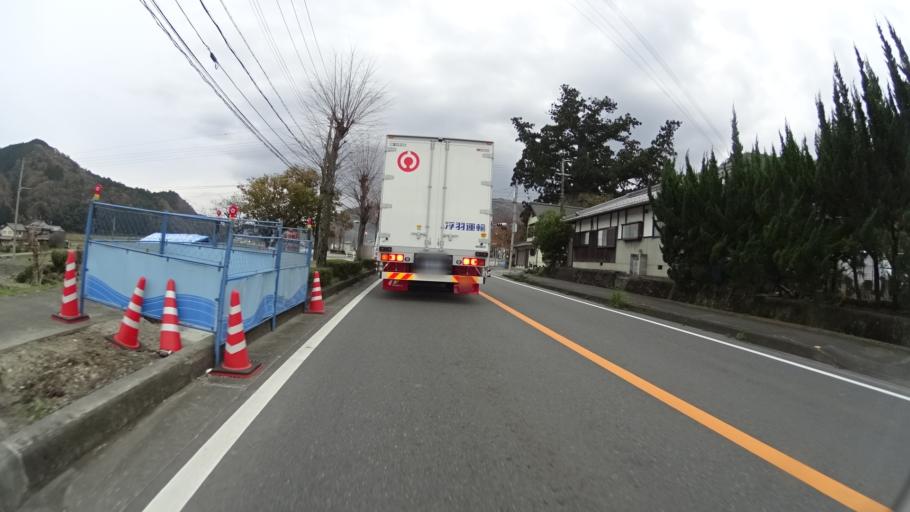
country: JP
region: Hyogo
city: Sasayama
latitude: 35.0723
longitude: 135.3354
